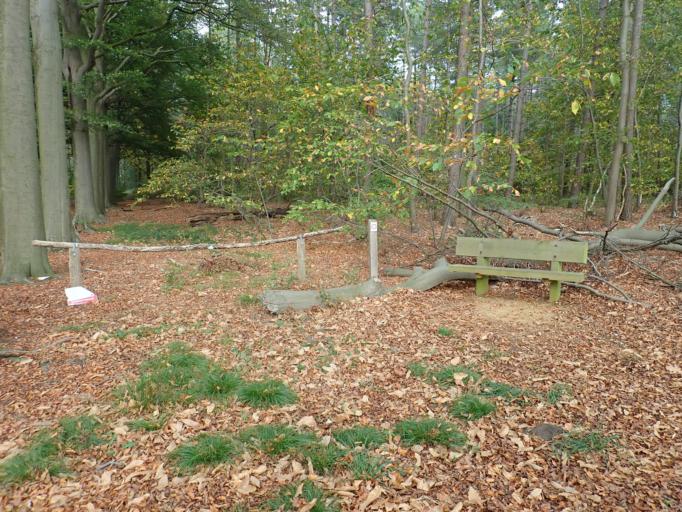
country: BE
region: Flanders
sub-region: Provincie Antwerpen
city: Herenthout
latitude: 51.1378
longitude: 4.7353
